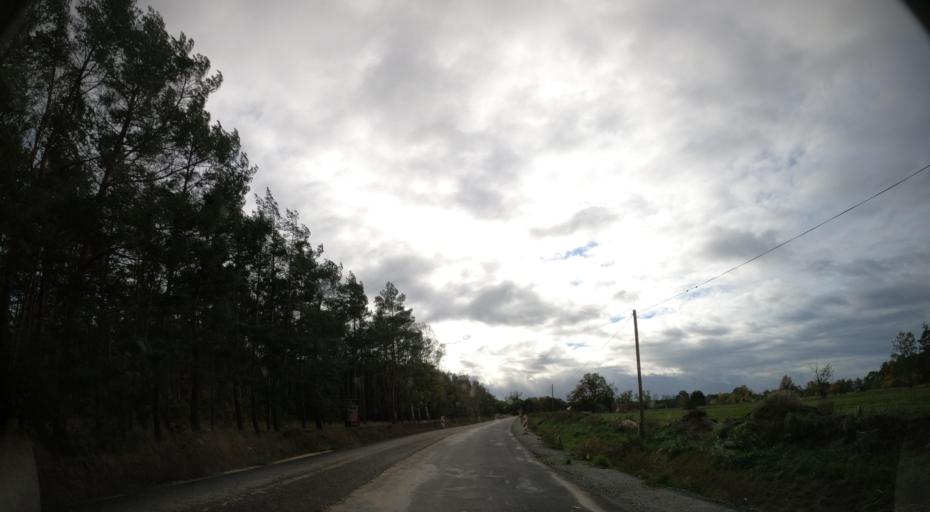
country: PL
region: West Pomeranian Voivodeship
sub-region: Powiat kamienski
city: Wolin
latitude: 53.7570
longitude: 14.6612
